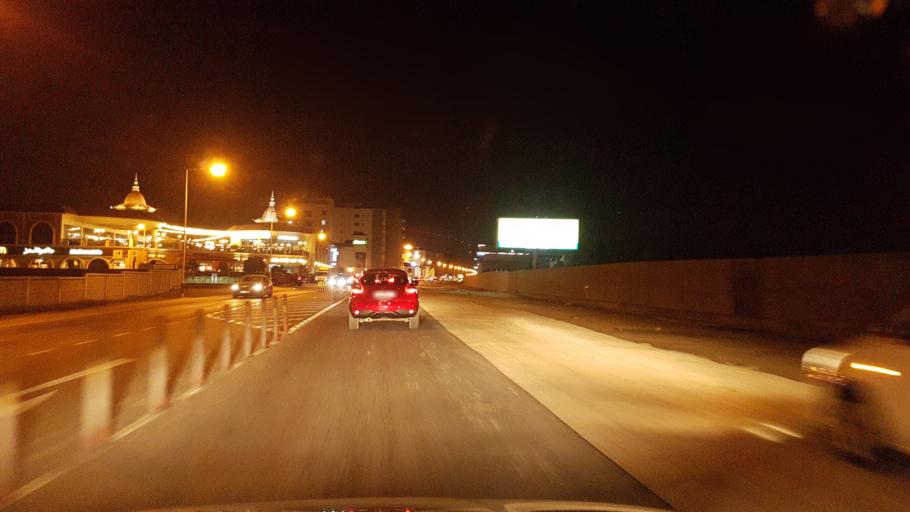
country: BH
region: Northern
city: Madinat `Isa
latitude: 26.1775
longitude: 50.4810
